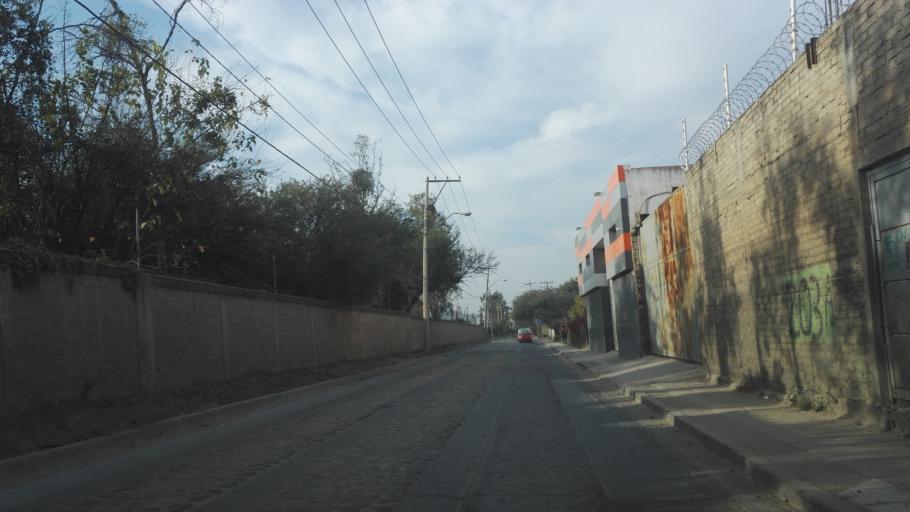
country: MX
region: Guanajuato
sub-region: Leon
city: Fraccionamiento Paraiso Real
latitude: 21.0897
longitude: -101.6099
